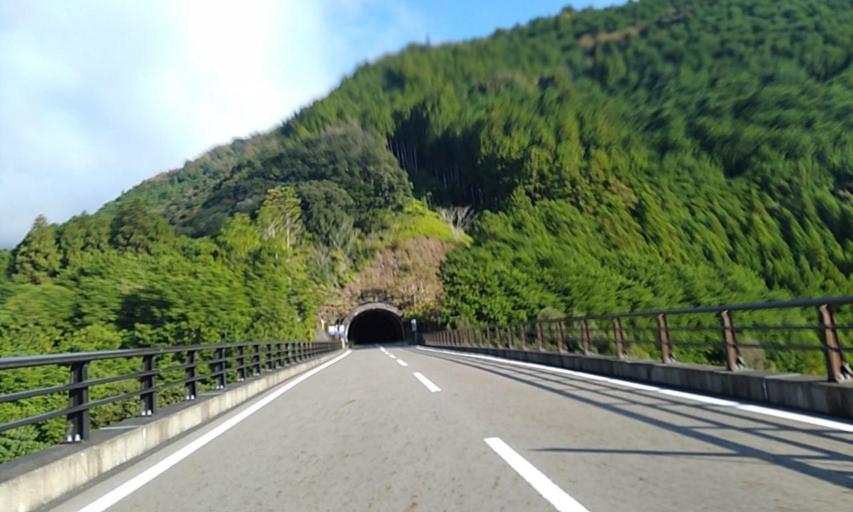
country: JP
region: Wakayama
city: Shingu
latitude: 33.8945
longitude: 135.8796
